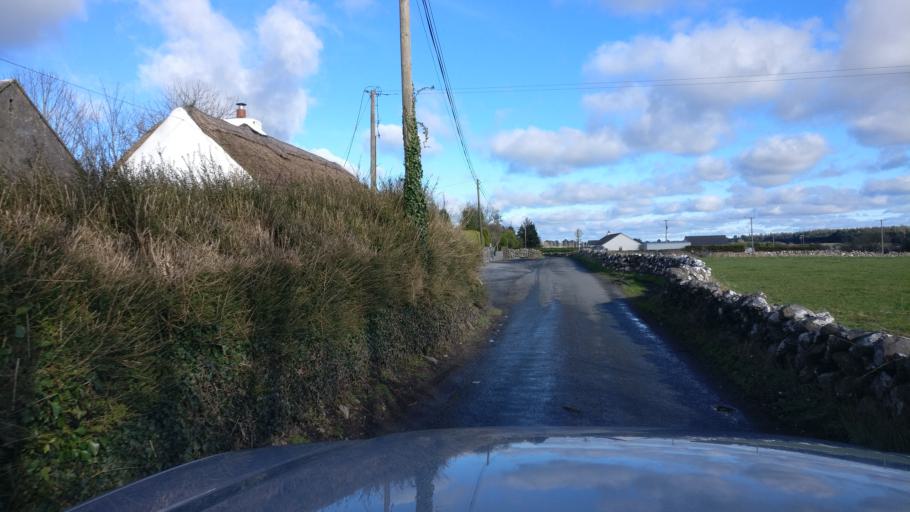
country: IE
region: Connaught
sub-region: County Galway
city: Oranmore
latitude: 53.2827
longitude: -8.8957
